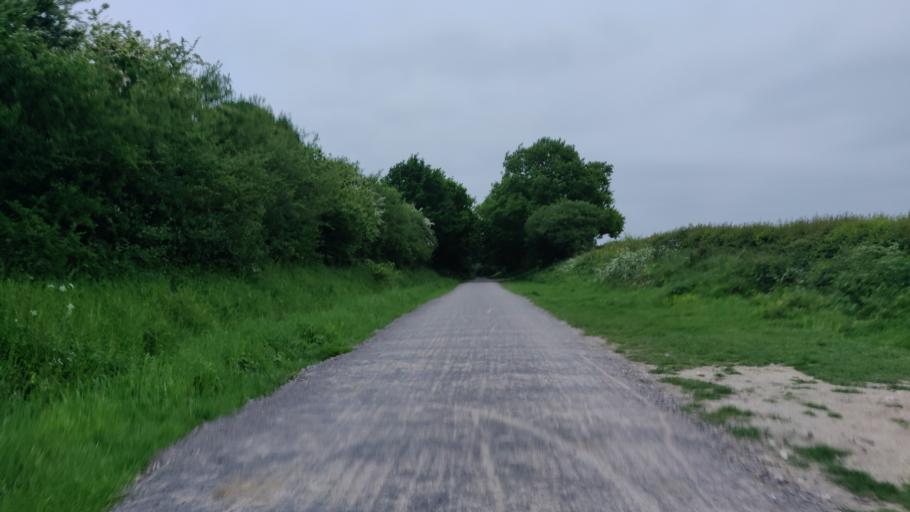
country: GB
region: England
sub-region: West Sussex
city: Partridge Green
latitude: 50.9708
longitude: -0.3155
